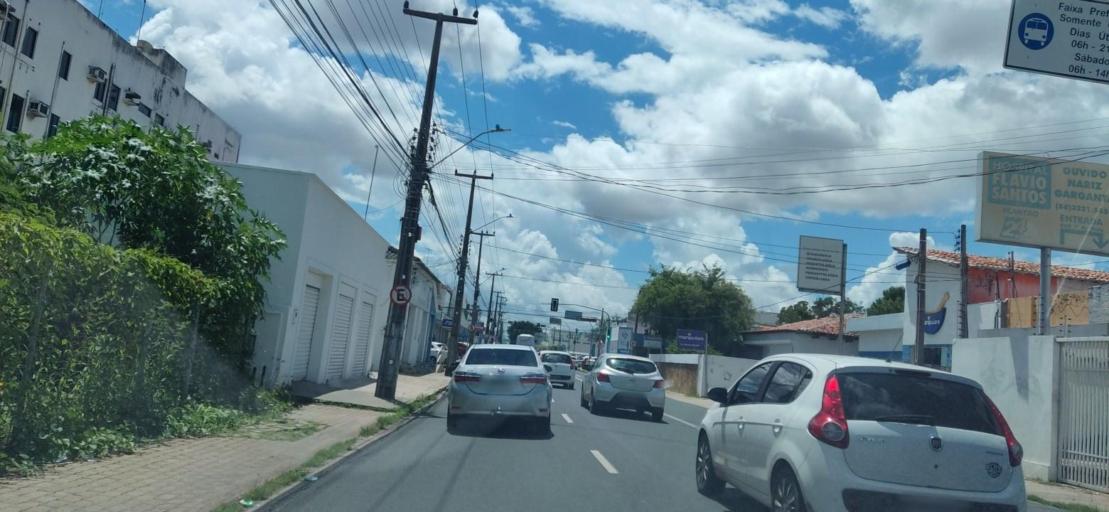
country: BR
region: Piaui
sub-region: Teresina
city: Teresina
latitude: -5.0892
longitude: -42.8050
